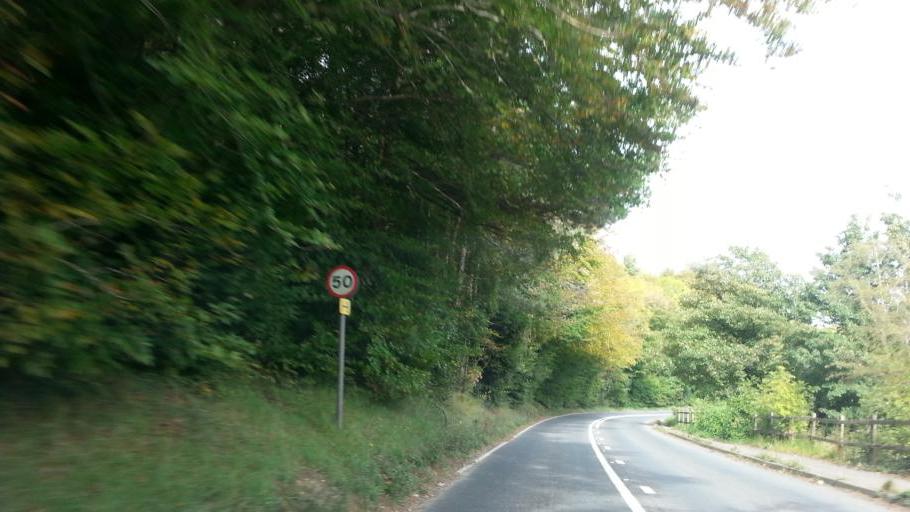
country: GB
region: England
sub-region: Gloucestershire
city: Painswick
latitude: 51.8022
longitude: -2.1920
